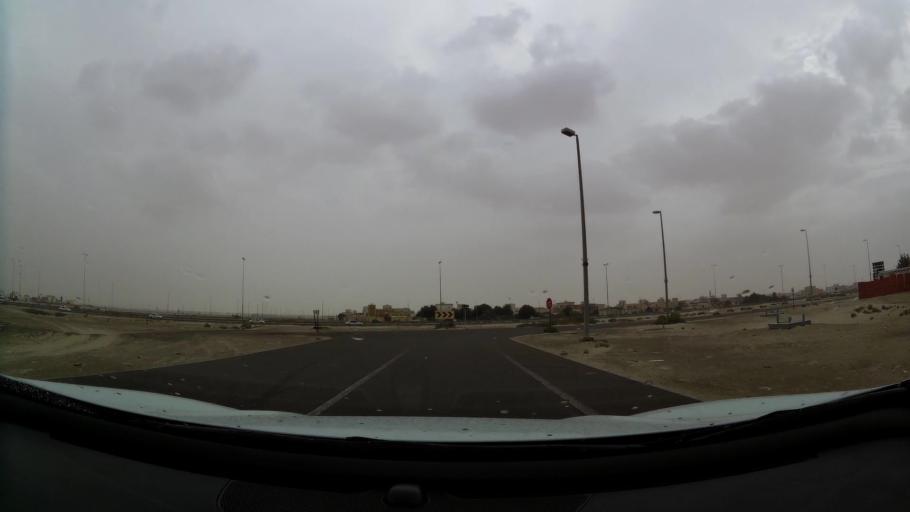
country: AE
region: Abu Dhabi
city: Abu Dhabi
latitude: 24.3634
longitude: 54.6585
